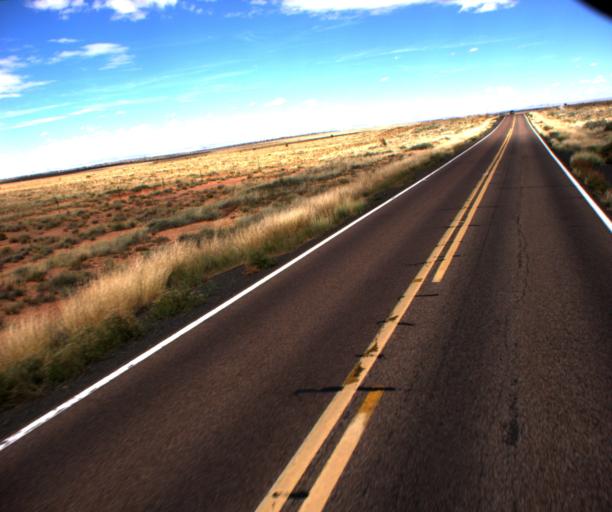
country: US
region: Arizona
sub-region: Navajo County
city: Holbrook
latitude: 34.7705
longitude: -110.2421
